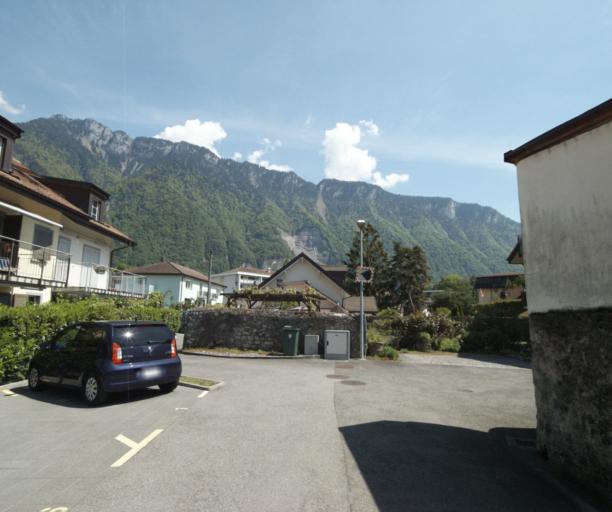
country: CH
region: Vaud
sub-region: Aigle District
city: Villeneuve
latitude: 46.3956
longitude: 6.9247
